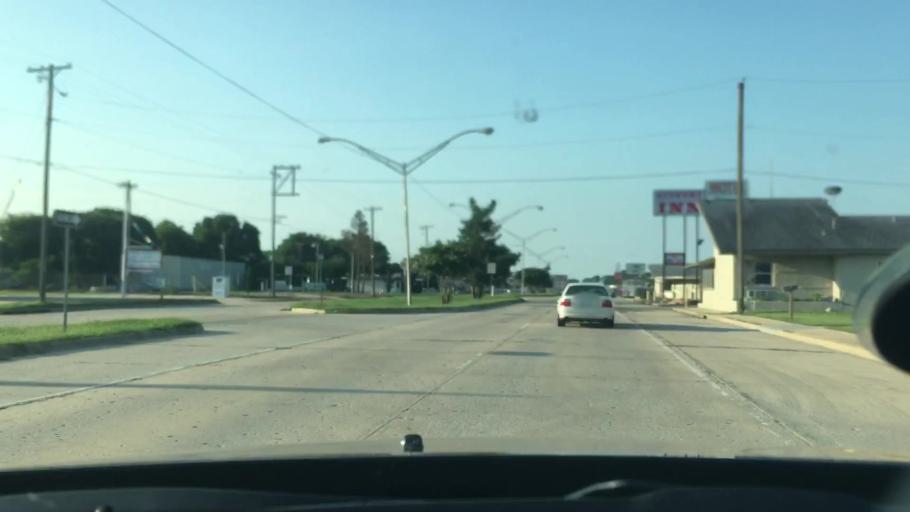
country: US
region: Oklahoma
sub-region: Pontotoc County
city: Ada
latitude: 34.7851
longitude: -96.6788
